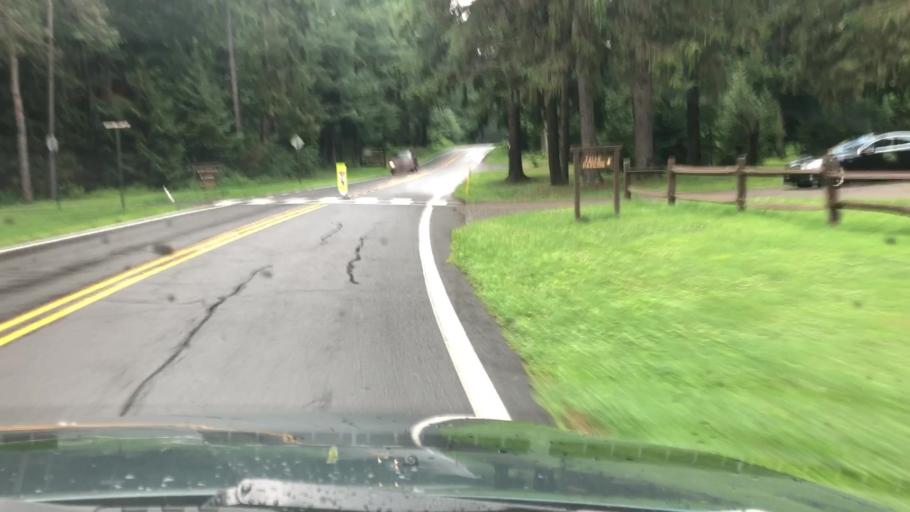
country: US
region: Pennsylvania
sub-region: Monroe County
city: Mountainhome
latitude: 41.3189
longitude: -75.2102
